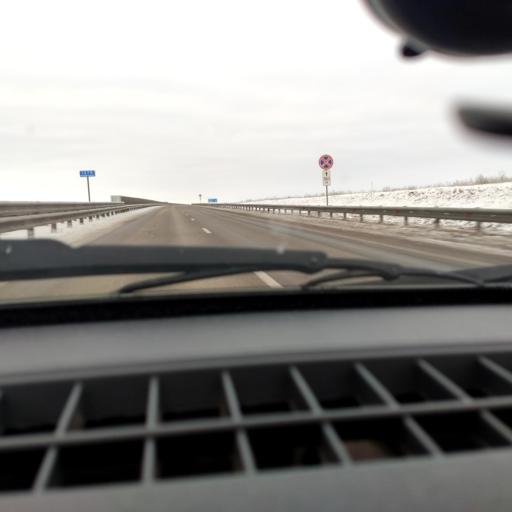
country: RU
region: Bashkortostan
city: Kushnarenkovo
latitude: 55.0822
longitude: 55.2658
